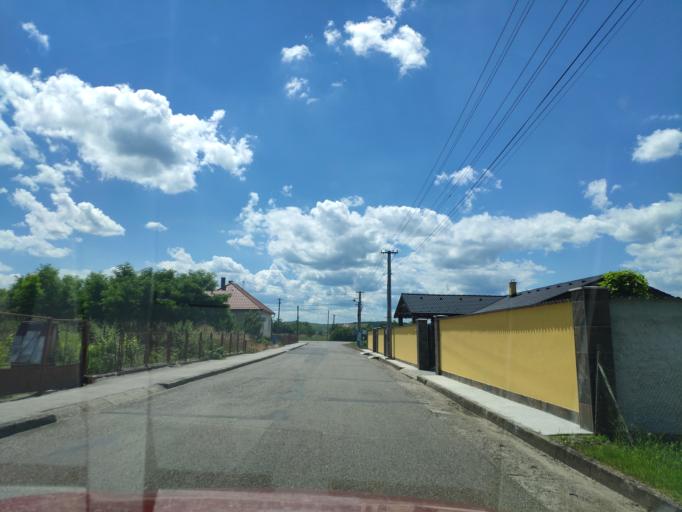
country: HU
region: Borsod-Abauj-Zemplen
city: Ozd
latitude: 48.3091
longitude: 20.2832
